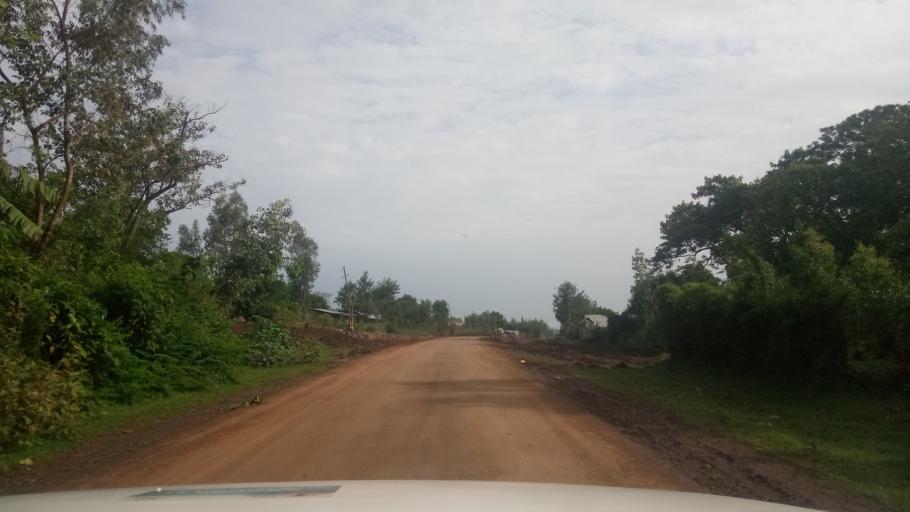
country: ET
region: Oromiya
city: Agaro
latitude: 7.8499
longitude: 36.6557
